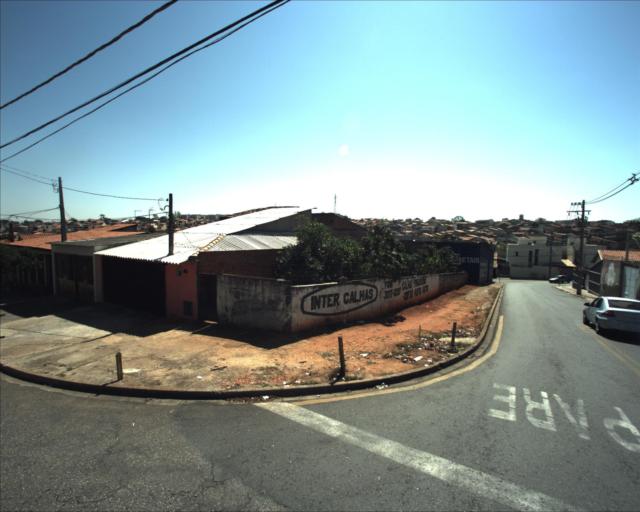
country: BR
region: Sao Paulo
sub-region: Sorocaba
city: Sorocaba
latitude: -23.4652
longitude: -47.4846
